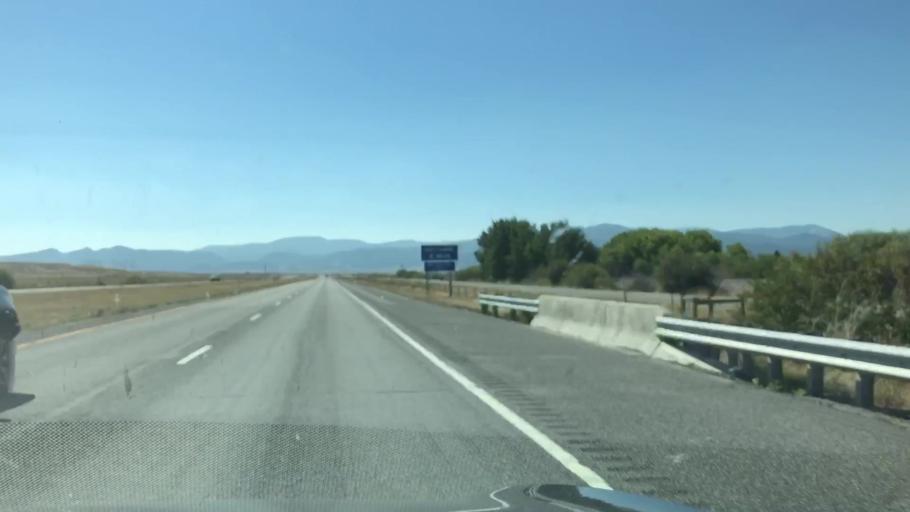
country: US
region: Montana
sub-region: Deer Lodge County
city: Warm Springs
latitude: 46.1244
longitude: -112.7972
